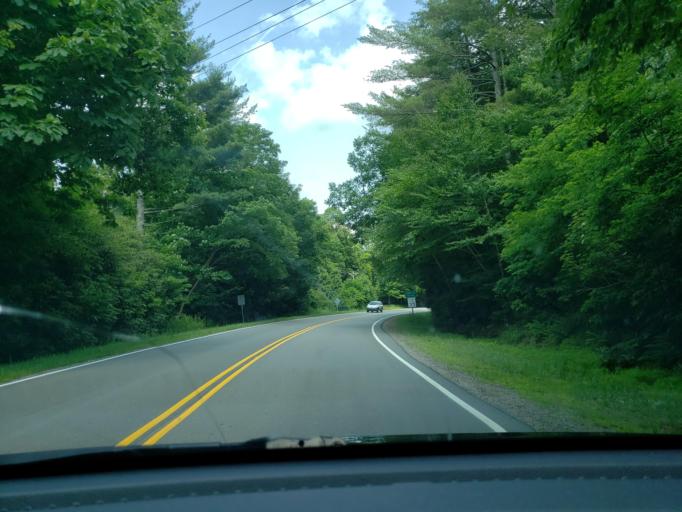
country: US
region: North Carolina
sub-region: Watauga County
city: Blowing Rock
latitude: 36.1398
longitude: -81.6913
